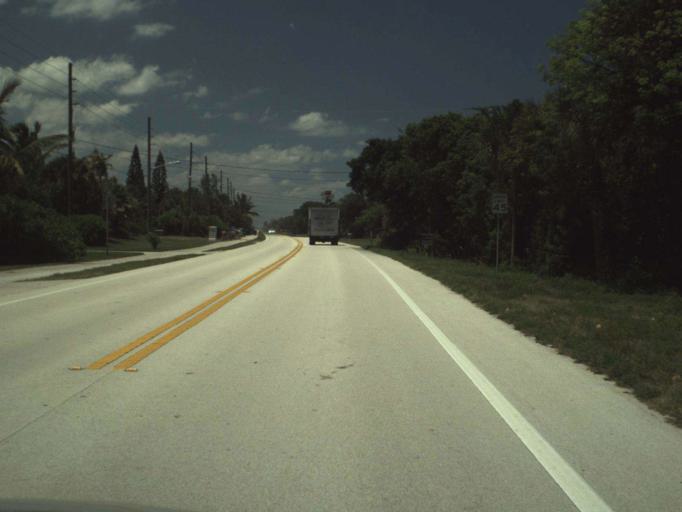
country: US
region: Florida
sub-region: Brevard County
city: Micco
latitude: 27.9117
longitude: -80.4769
